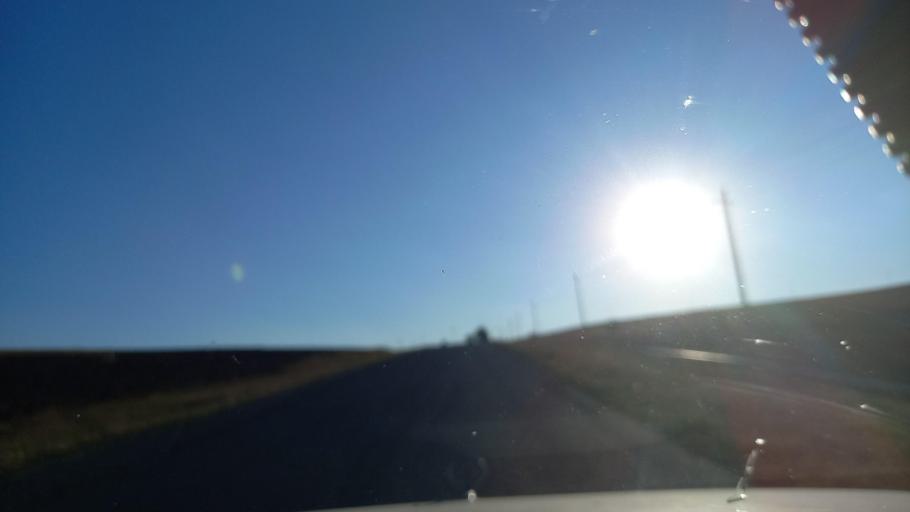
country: AZ
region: Shamkir Rayon
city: Shamkhor
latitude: 40.7597
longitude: 45.9113
